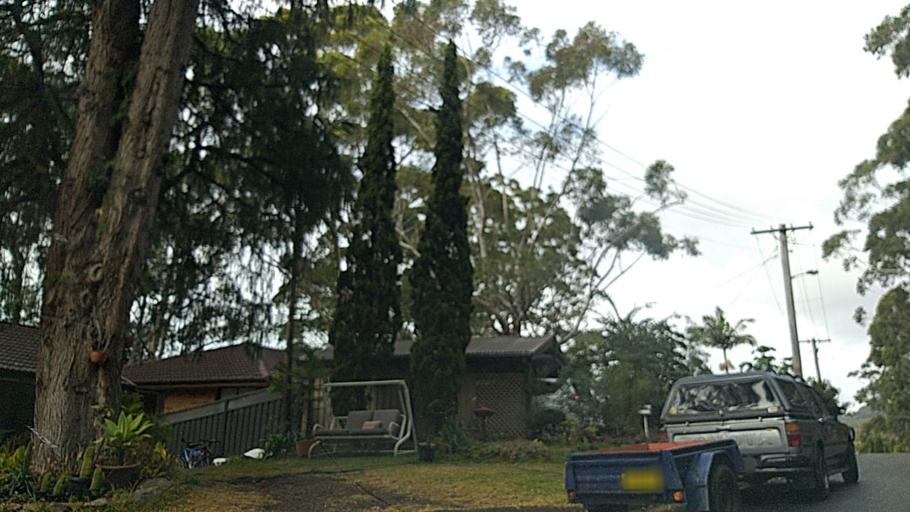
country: AU
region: New South Wales
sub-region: Wollongong
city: Bulli
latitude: -34.3121
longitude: 150.9092
